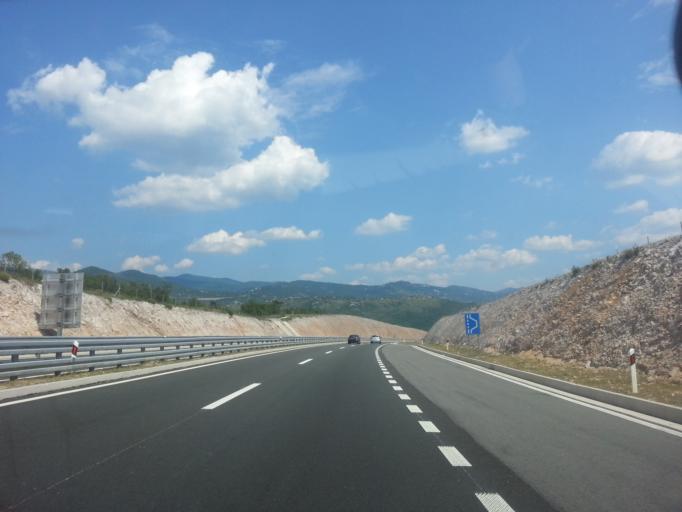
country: HR
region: Primorsko-Goranska
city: Bakar
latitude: 45.3111
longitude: 14.5423
